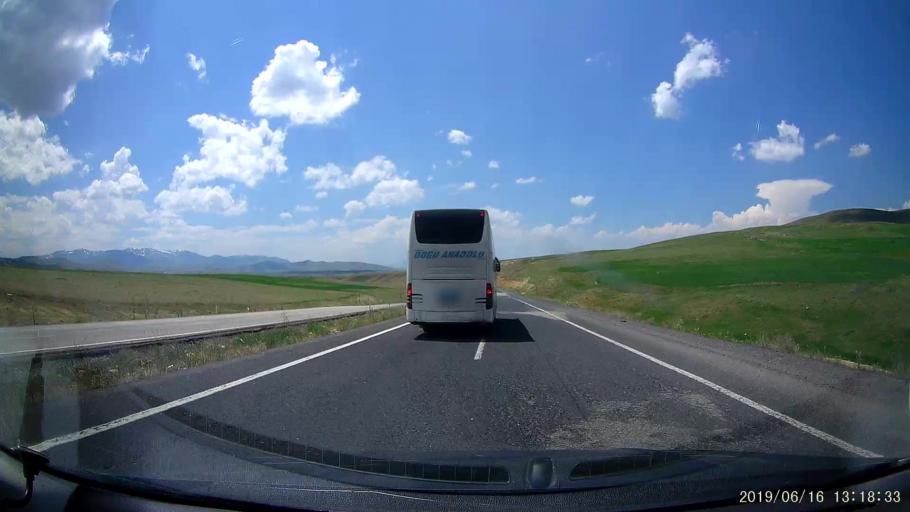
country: TR
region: Agri
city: Taslicay
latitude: 39.6310
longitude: 43.4285
